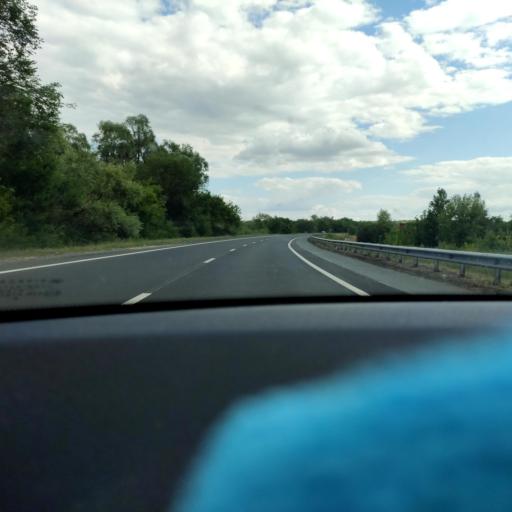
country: RU
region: Samara
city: Novosemeykino
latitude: 53.4159
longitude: 50.3354
